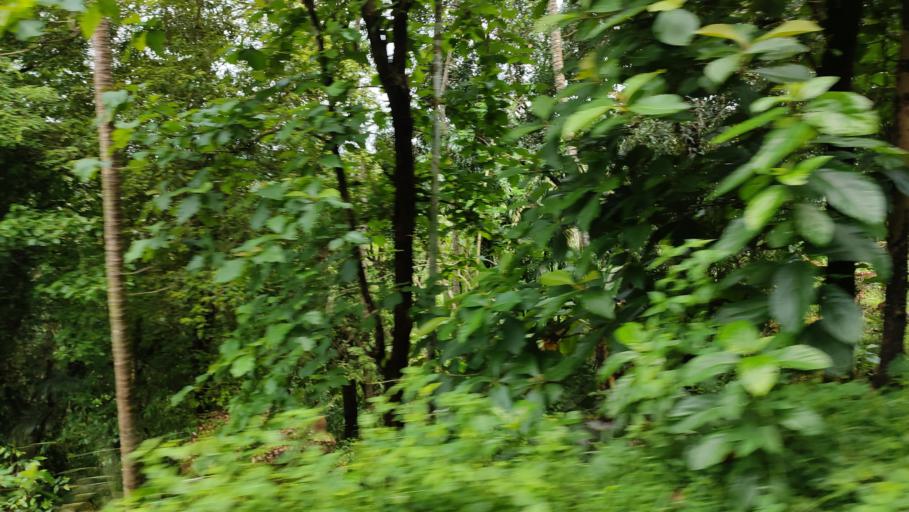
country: IN
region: Kerala
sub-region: Kasaragod District
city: Nileshwar
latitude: 12.2838
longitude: 75.2637
